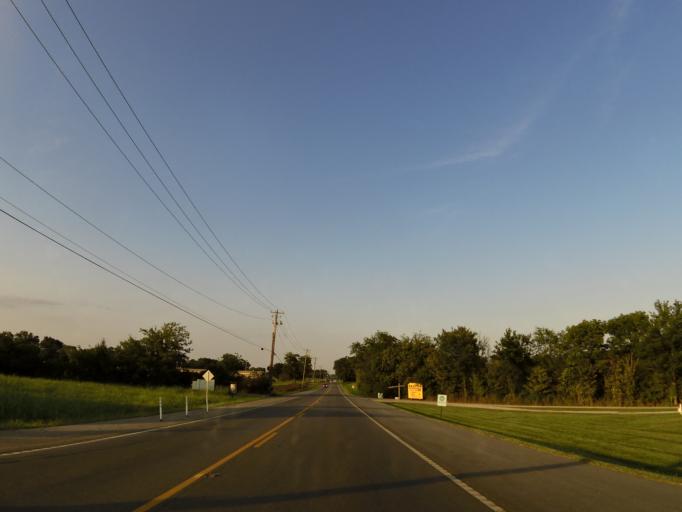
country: US
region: Tennessee
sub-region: Monroe County
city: Sweetwater
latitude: 35.5787
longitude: -84.4867
